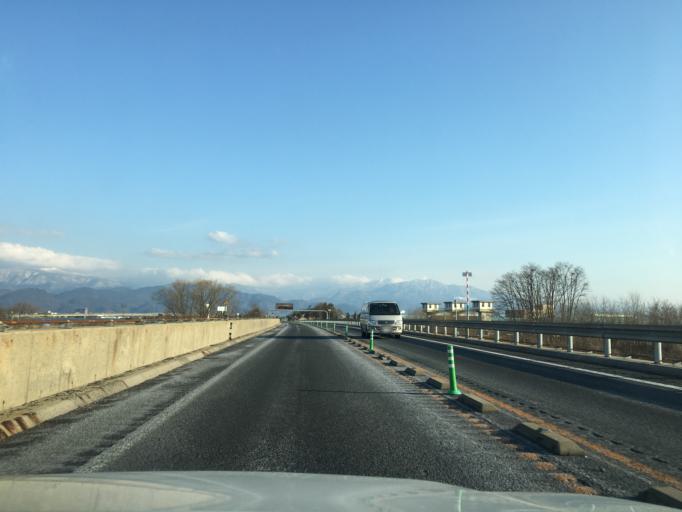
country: JP
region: Yamagata
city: Sagae
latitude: 38.3195
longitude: 140.3027
